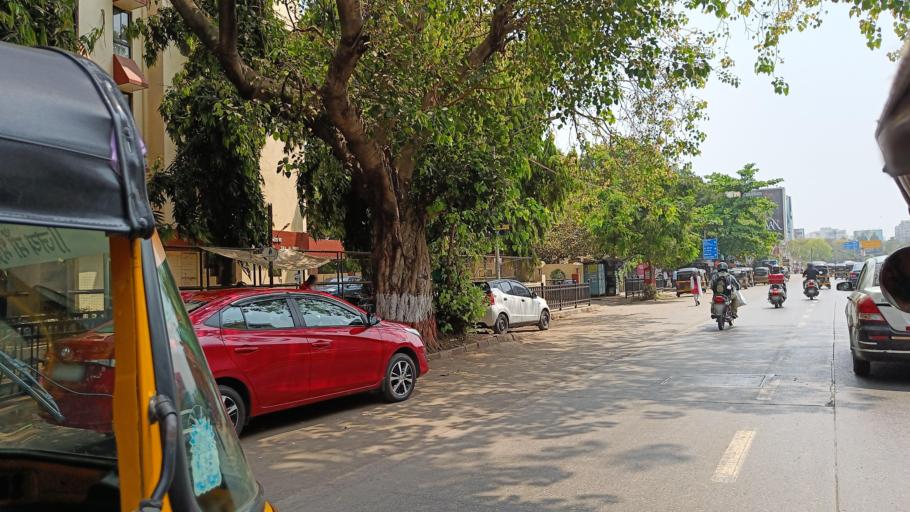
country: IN
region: Maharashtra
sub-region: Mumbai Suburban
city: Mumbai
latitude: 19.0858
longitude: 72.8292
